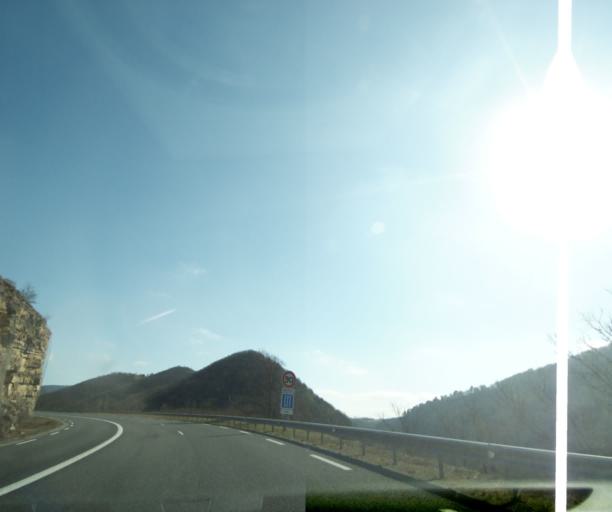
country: FR
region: Midi-Pyrenees
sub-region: Departement de l'Aveyron
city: Saint-Affrique
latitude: 43.9557
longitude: 2.9516
